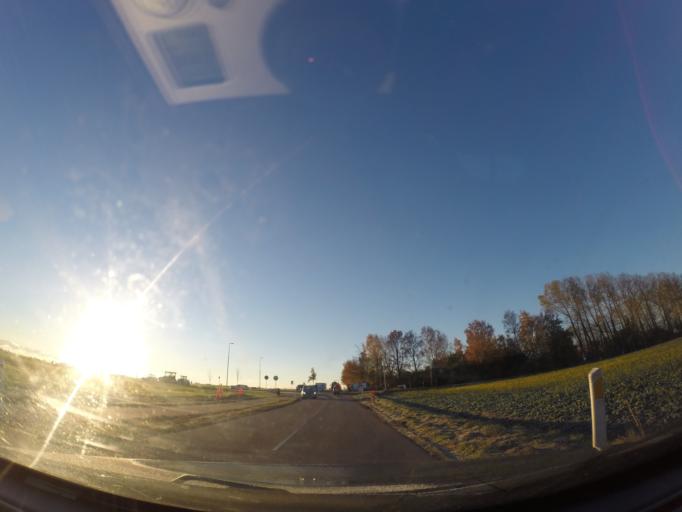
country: DK
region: Capital Region
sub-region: Hoje-Taastrup Kommune
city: Taastrup
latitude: 55.6791
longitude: 12.2524
